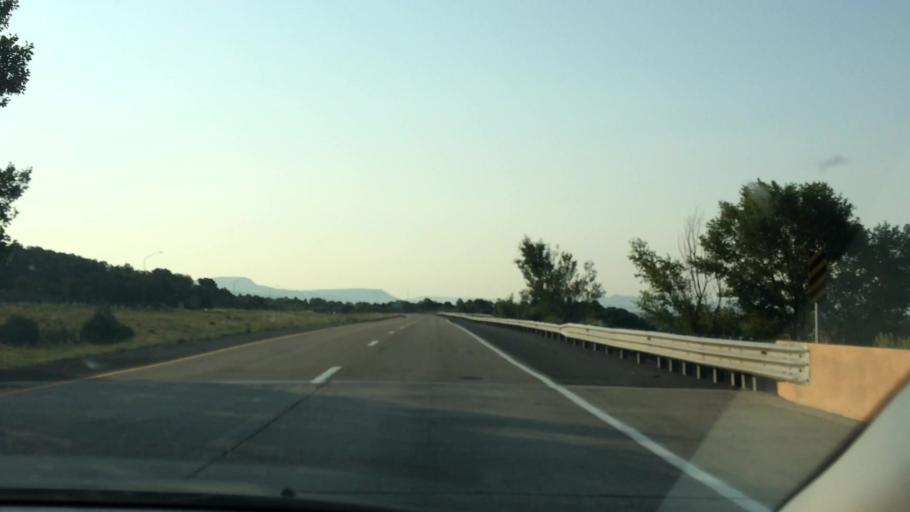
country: US
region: New Mexico
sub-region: Colfax County
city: Raton
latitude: 36.9177
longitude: -104.4462
